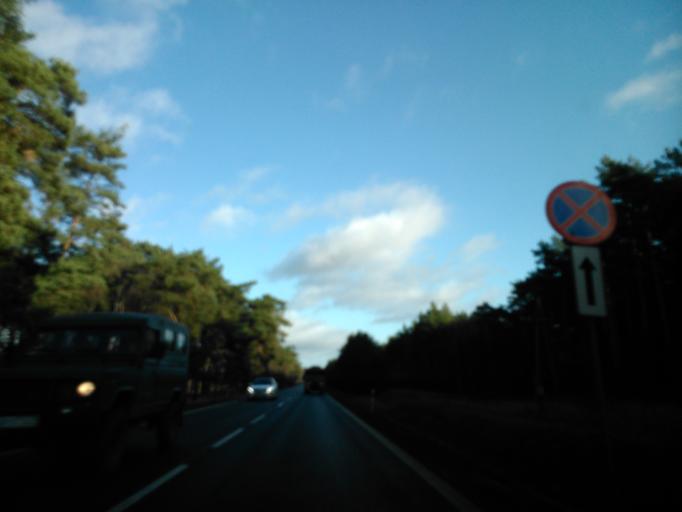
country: PL
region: Kujawsko-Pomorskie
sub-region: Powiat torunski
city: Wielka Nieszawka
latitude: 52.9271
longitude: 18.5040
